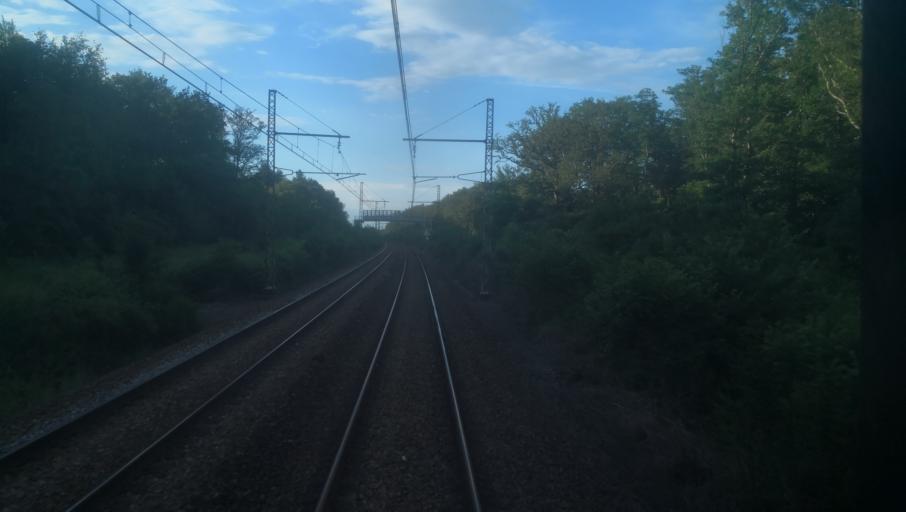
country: FR
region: Centre
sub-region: Departement de l'Indre
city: Luant
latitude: 46.7403
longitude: 1.5926
